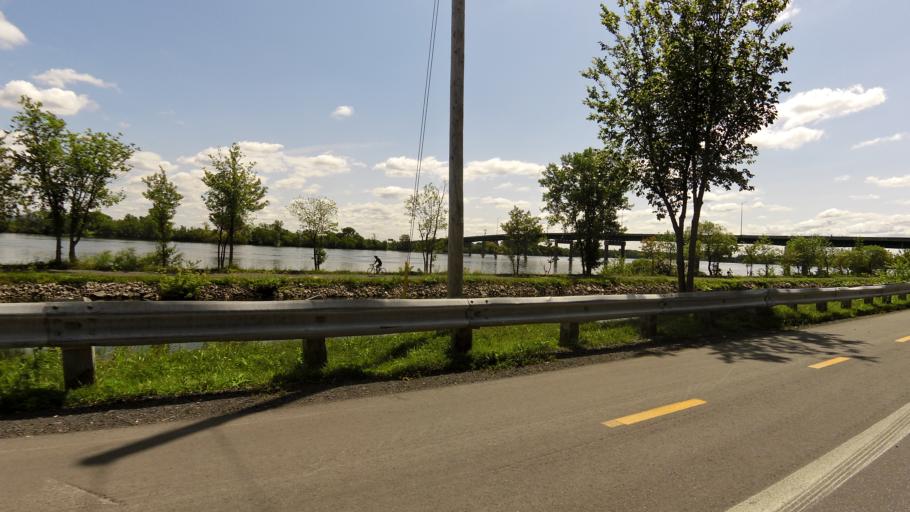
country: CA
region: Quebec
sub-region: Monteregie
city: Saint-Jean-sur-Richelieu
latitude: 45.3288
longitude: -73.2637
